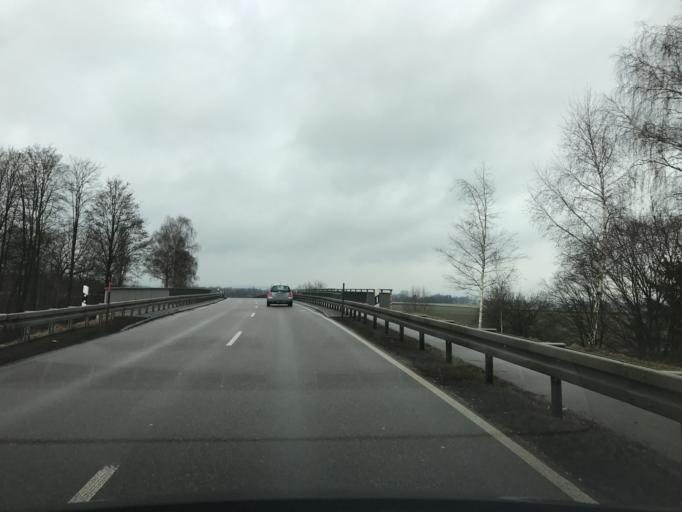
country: DE
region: Baden-Wuerttemberg
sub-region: Tuebingen Region
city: Laupheim
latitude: 48.2489
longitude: 9.8574
